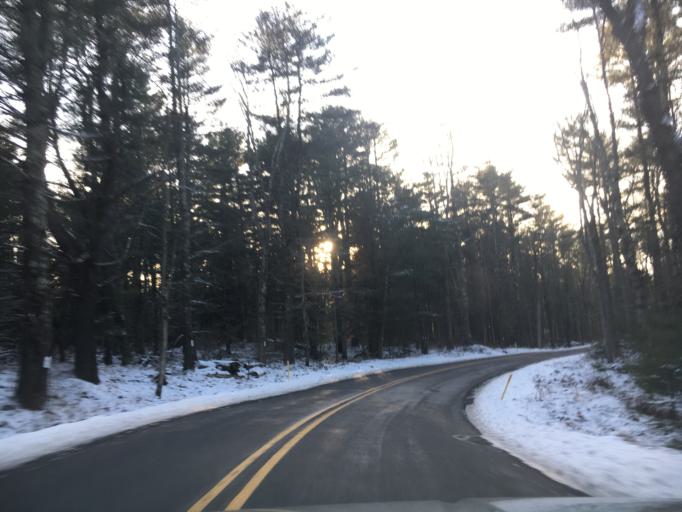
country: US
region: Pennsylvania
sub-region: Pike County
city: Hemlock Farms
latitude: 41.3721
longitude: -75.1134
